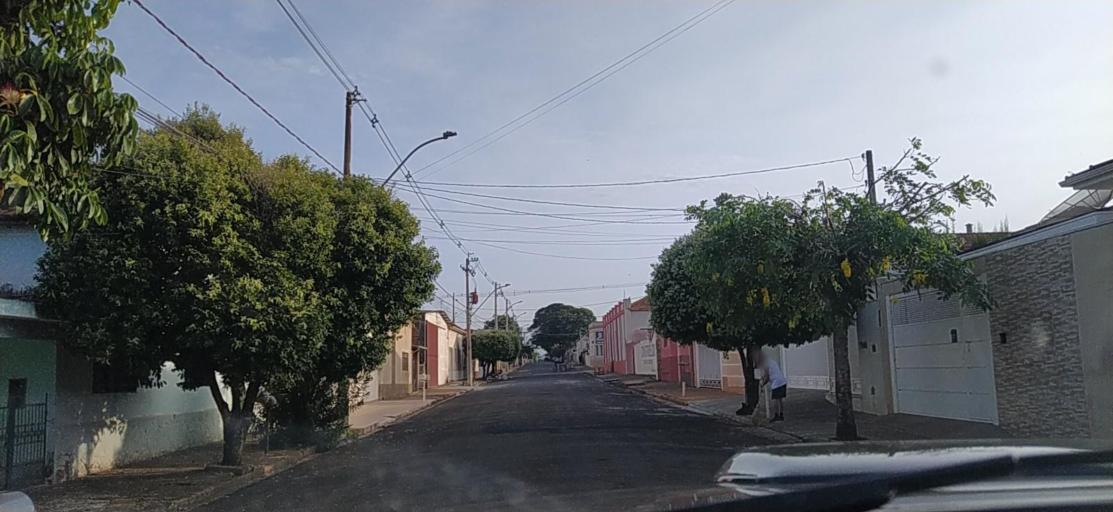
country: BR
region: Sao Paulo
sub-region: Pindorama
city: Pindorama
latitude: -21.1902
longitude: -48.9036
